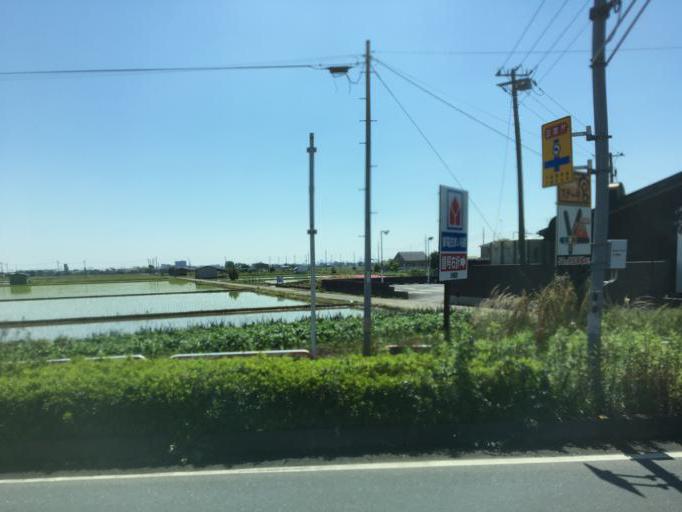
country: JP
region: Saitama
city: Kawagoe
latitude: 35.9353
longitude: 139.4865
